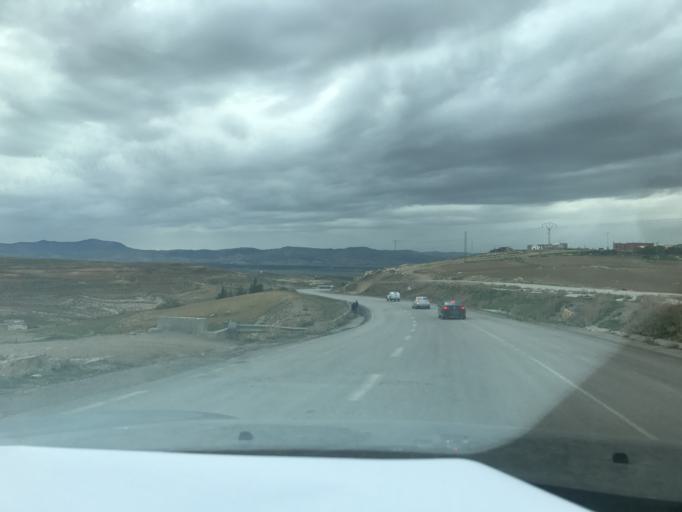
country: TN
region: Silyanah
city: Siliana
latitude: 36.0922
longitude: 9.4686
